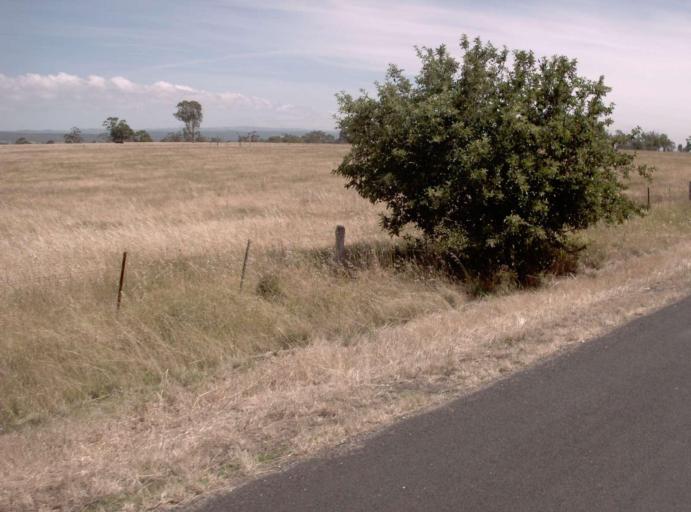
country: AU
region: Victoria
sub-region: Wellington
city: Heyfield
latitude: -38.1345
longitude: 146.8047
